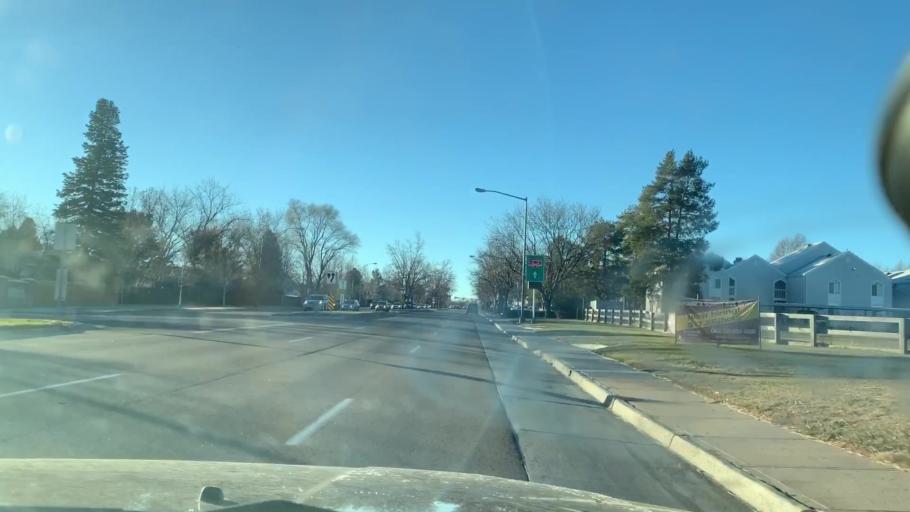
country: US
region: Colorado
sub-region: Arapahoe County
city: Cherry Hills Village
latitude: 39.6568
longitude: -104.9130
